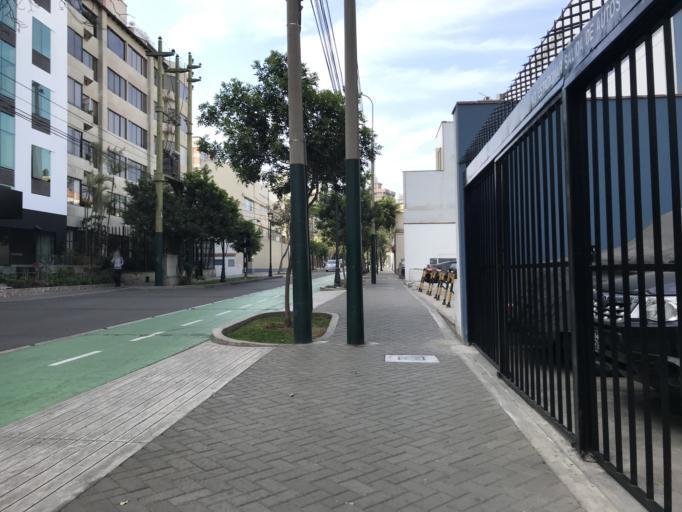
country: PE
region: Lima
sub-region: Lima
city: San Isidro
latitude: -12.1028
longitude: -77.0376
